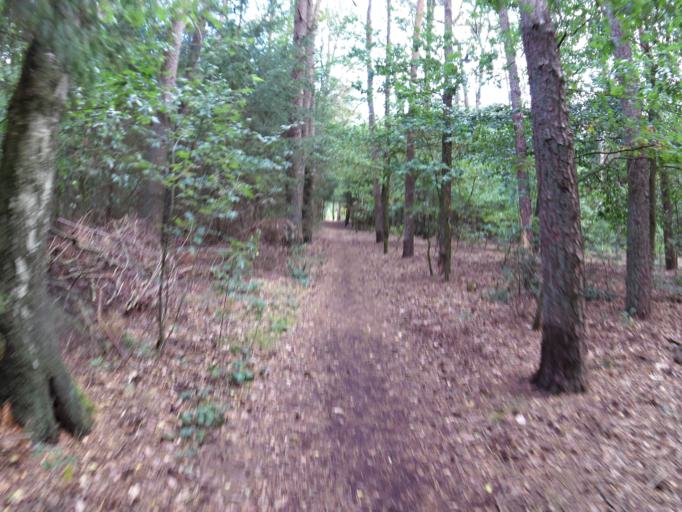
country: DE
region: Lower Saxony
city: Heeslingen
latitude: 53.3155
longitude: 9.3145
